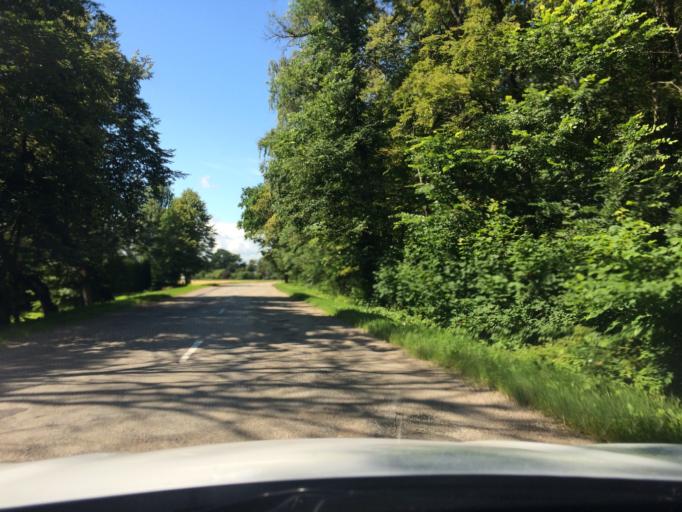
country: LV
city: Tervete
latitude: 56.5340
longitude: 23.5225
